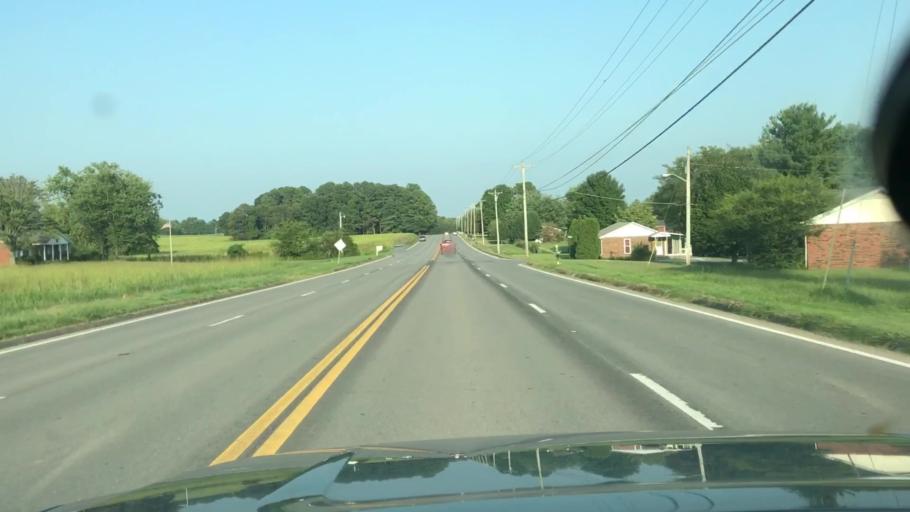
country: US
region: Tennessee
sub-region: Sumner County
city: Portland
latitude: 36.5779
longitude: -86.4878
